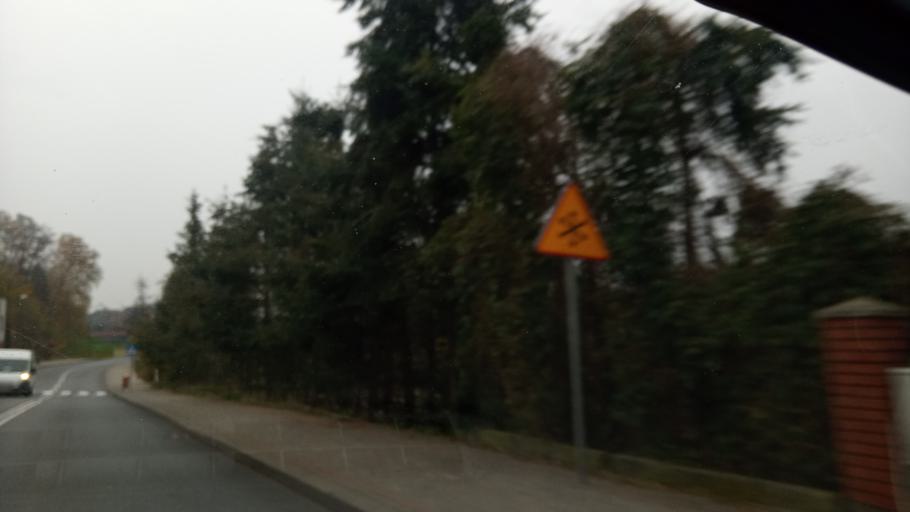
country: PL
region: Kujawsko-Pomorskie
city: Kamien Krajenski
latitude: 53.5370
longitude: 17.5221
